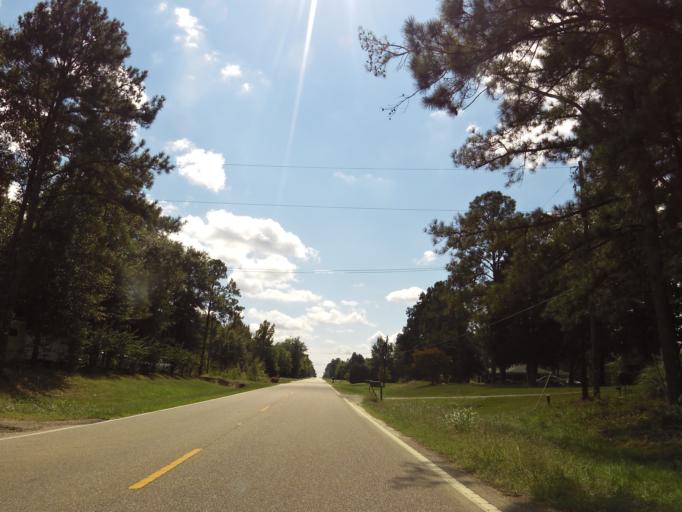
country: US
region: Alabama
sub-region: Dallas County
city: Selma
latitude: 32.4404
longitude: -87.0836
